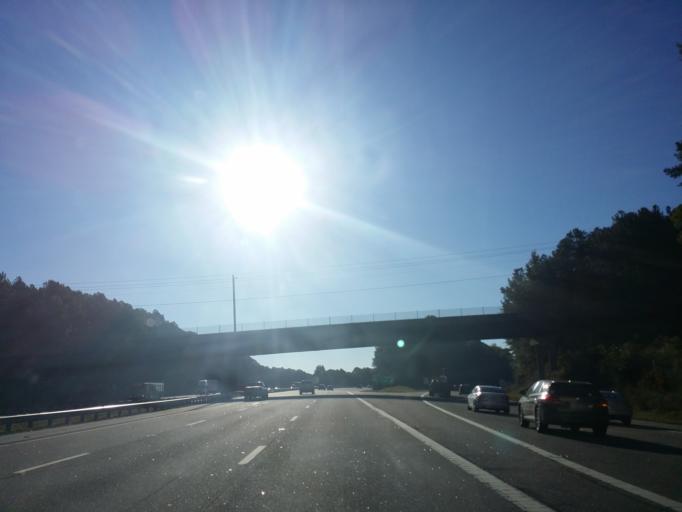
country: US
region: North Carolina
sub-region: Wake County
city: Cary
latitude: 35.8205
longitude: -78.7439
